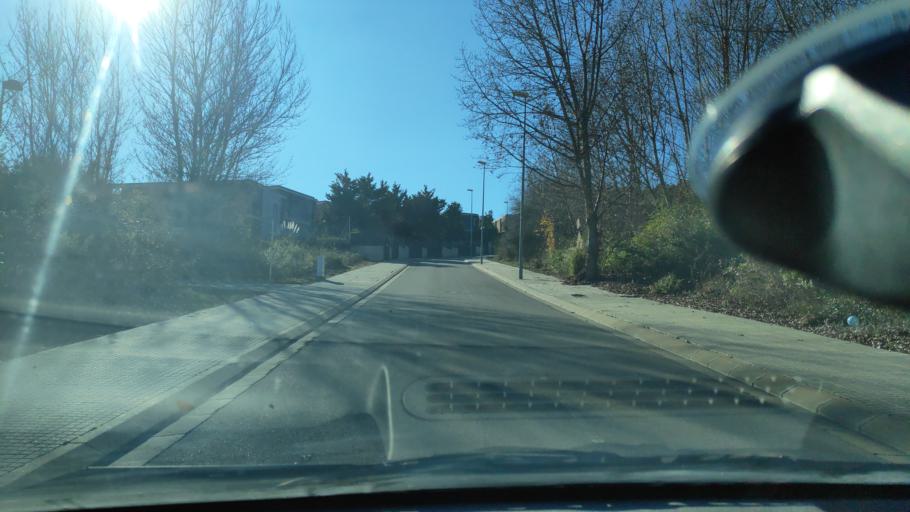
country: ES
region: Catalonia
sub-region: Provincia de Barcelona
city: Sant Quirze del Valles
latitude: 41.5339
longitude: 2.0573
